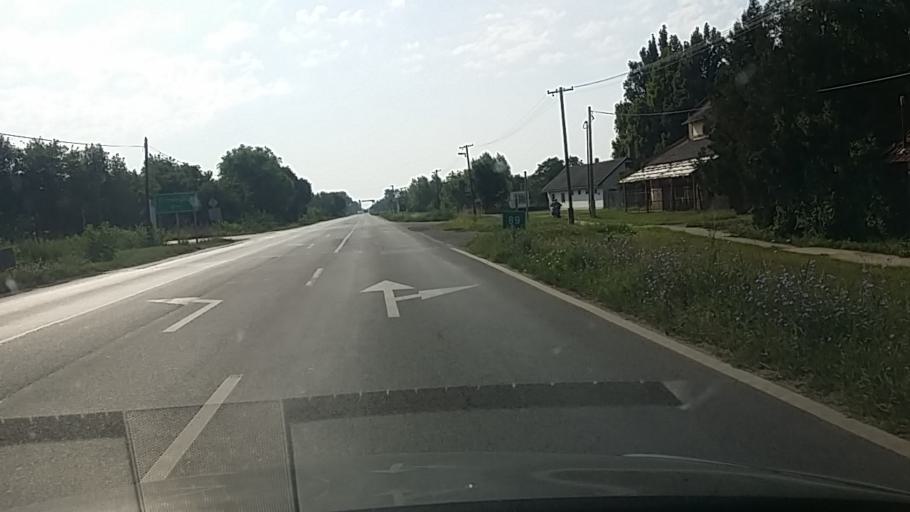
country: HU
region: Bekes
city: Kondoros
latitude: 46.8009
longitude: 20.7121
